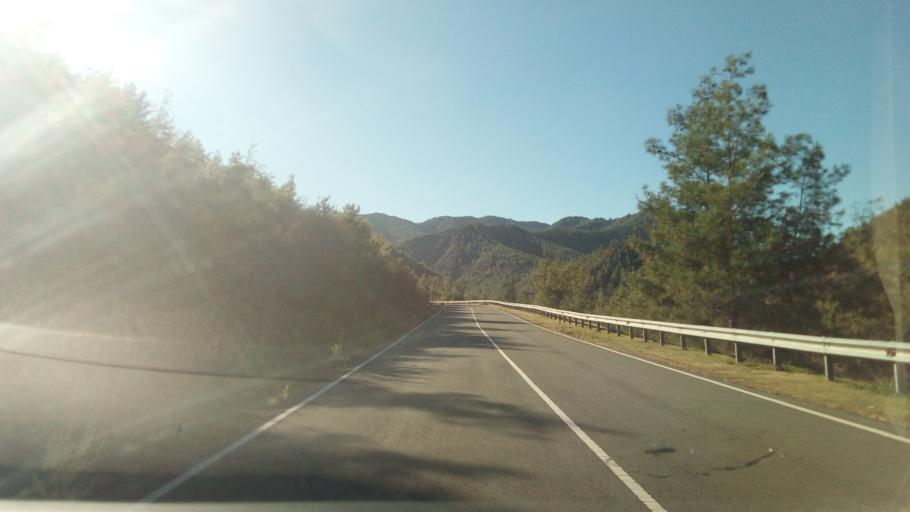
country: CY
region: Lefkosia
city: Lefka
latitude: 35.0951
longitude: 32.7615
